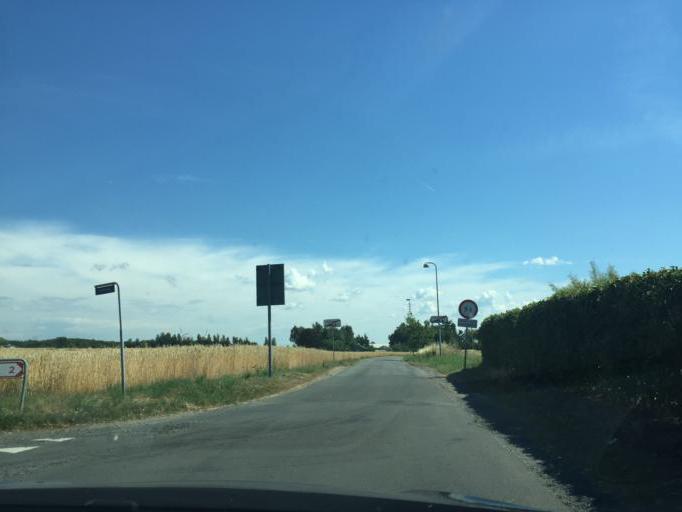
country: DK
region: South Denmark
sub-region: Odense Kommune
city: Bellinge
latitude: 55.3380
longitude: 10.3609
